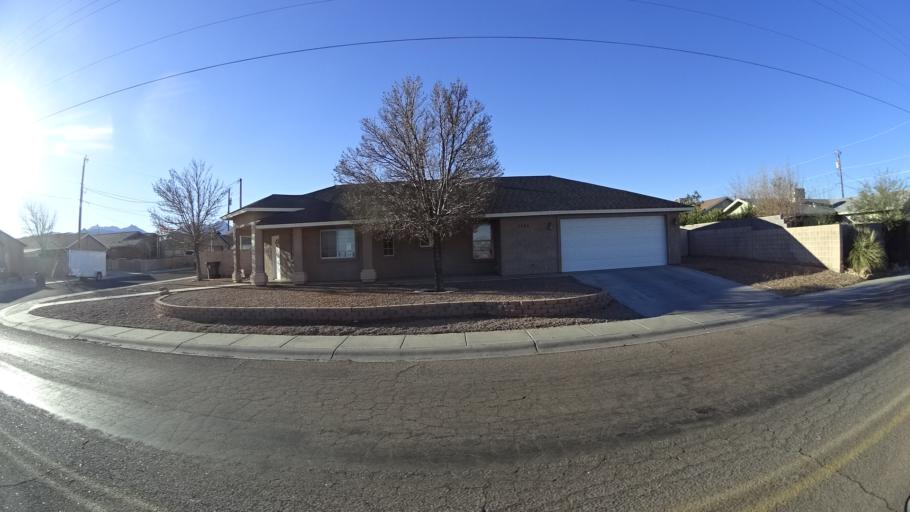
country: US
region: Arizona
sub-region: Mohave County
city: New Kingman-Butler
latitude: 35.2211
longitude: -114.0011
